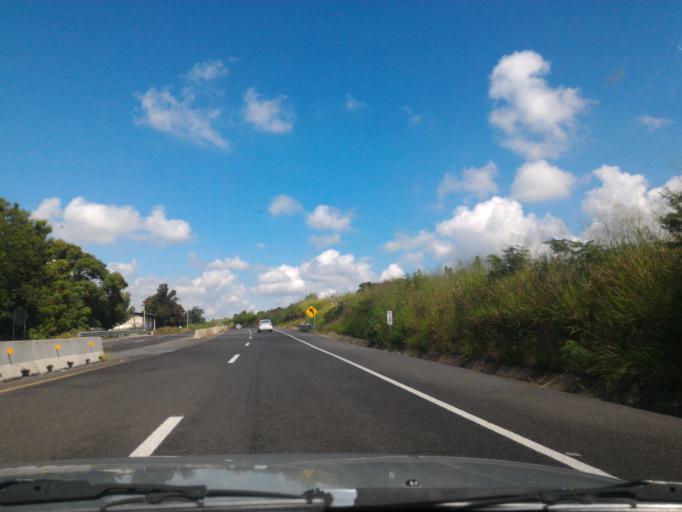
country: MX
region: Jalisco
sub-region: Tala
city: Los Ruisenores
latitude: 20.7437
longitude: -103.6378
